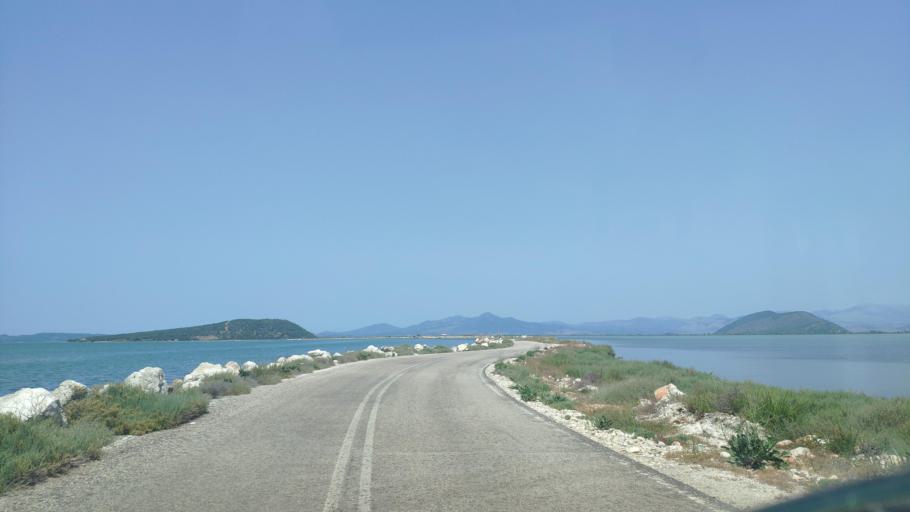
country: GR
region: Epirus
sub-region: Nomos Artas
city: Aneza
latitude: 39.0288
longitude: 20.9014
